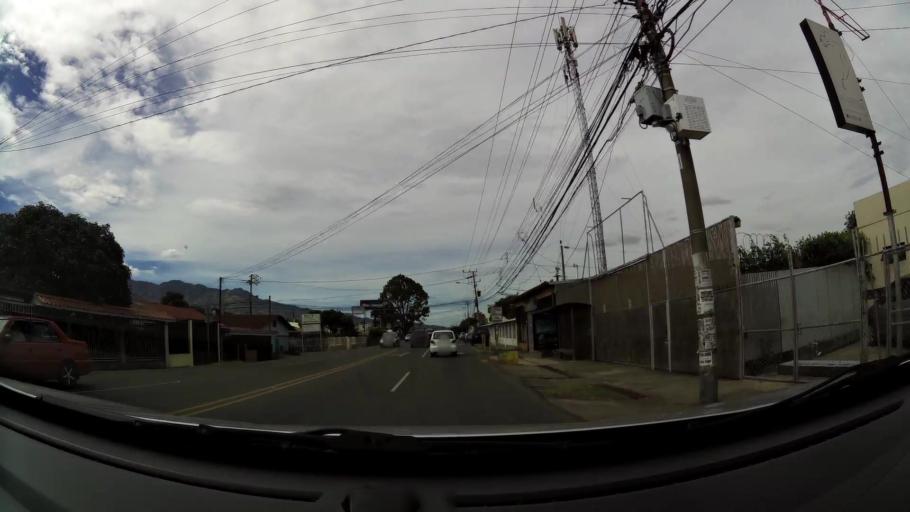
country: CR
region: San Jose
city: Curridabat
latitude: 9.8982
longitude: -84.0522
